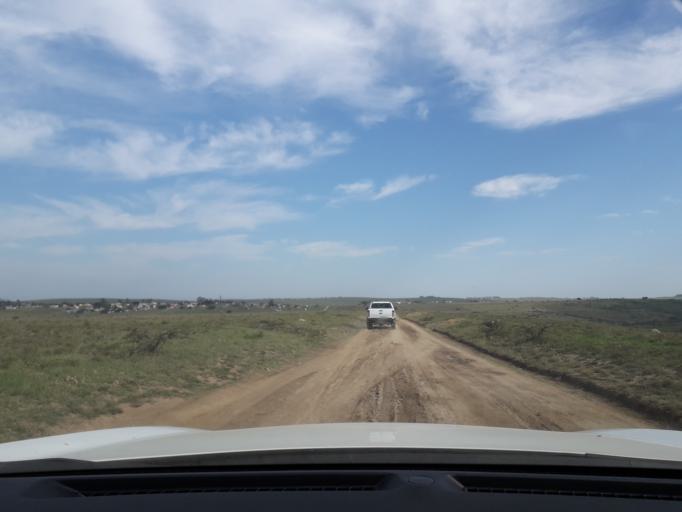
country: ZA
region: Eastern Cape
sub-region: Buffalo City Metropolitan Municipality
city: Bhisho
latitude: -32.9930
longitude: 27.3470
